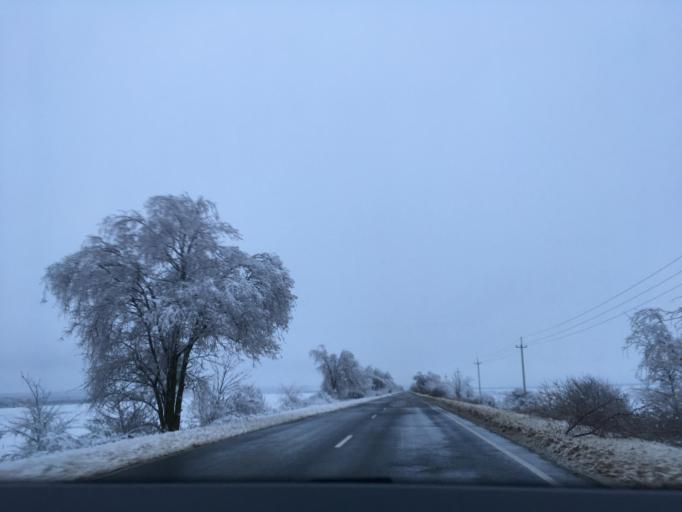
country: RU
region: Voronezj
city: Verkhniy Mamon
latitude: 50.0219
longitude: 40.0941
